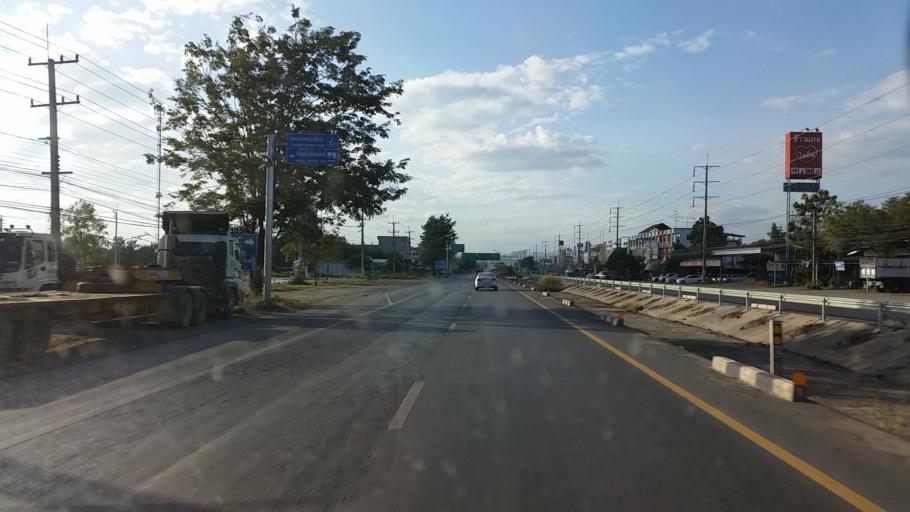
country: TH
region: Lop Buri
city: Phatthana Nikhom
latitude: 14.8511
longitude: 100.9098
